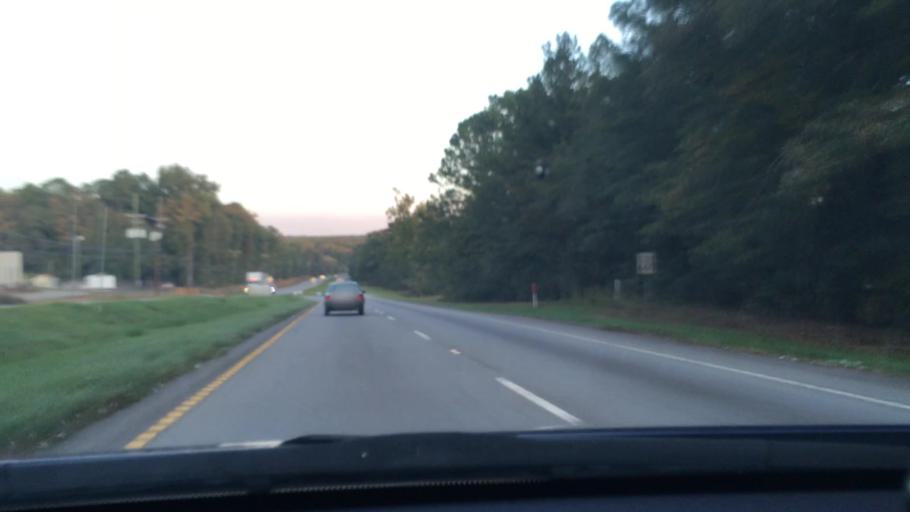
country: US
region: South Carolina
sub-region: Richland County
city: Hopkins
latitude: 33.9519
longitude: -80.8380
